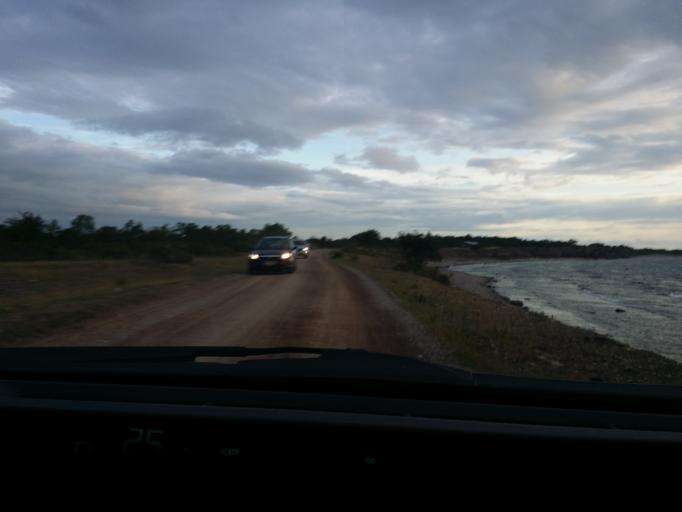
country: SE
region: Kalmar
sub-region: Borgholms Kommun
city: Borgholm
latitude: 57.2081
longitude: 16.9332
